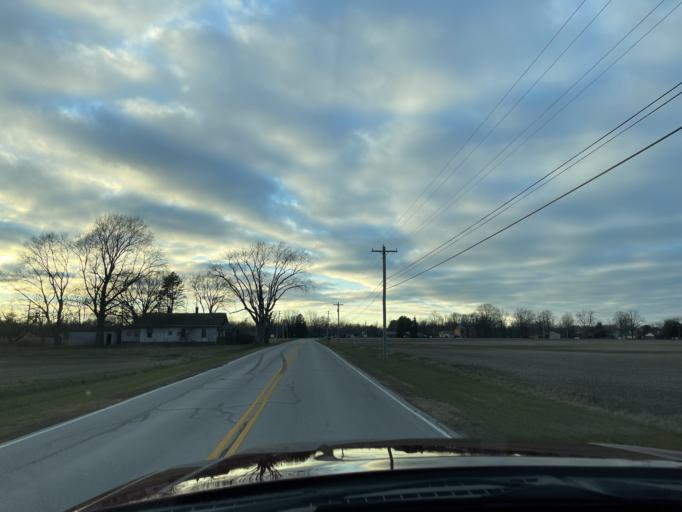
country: US
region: Indiana
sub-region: Hendricks County
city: Avon
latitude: 39.7724
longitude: -86.4343
